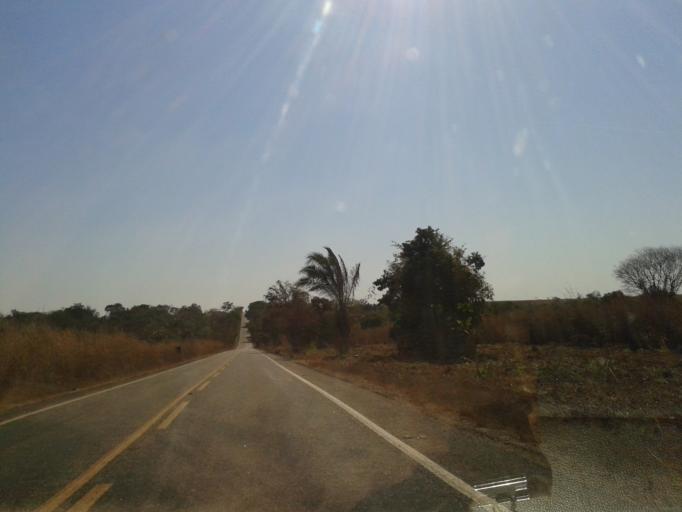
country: BR
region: Goias
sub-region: Mozarlandia
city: Mozarlandia
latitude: -14.4768
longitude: -50.4740
